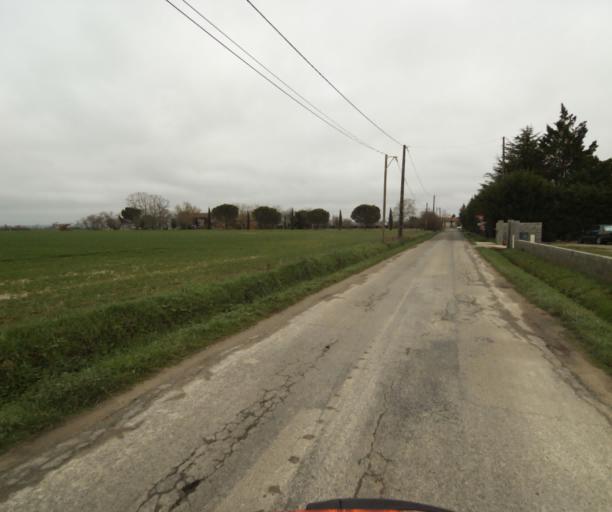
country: FR
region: Midi-Pyrenees
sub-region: Departement de l'Ariege
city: Saverdun
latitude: 43.2594
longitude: 1.5288
